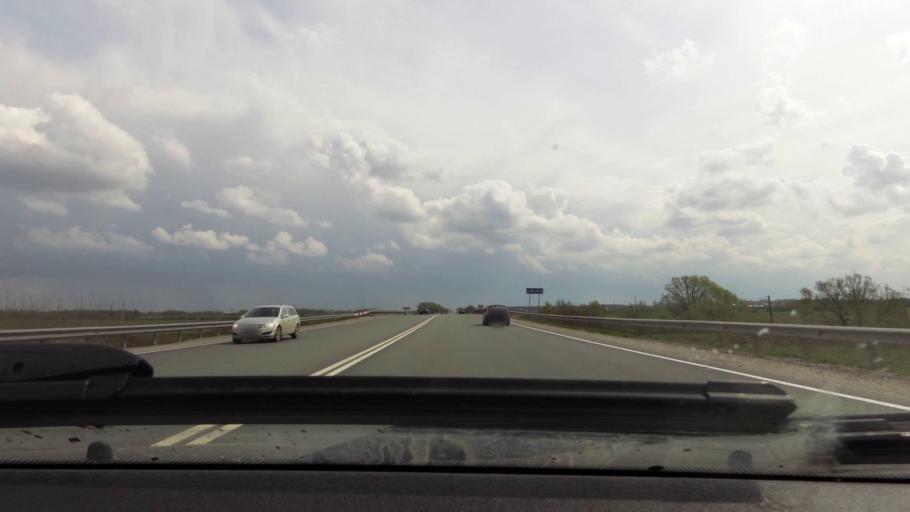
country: RU
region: Rjazan
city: Bagramovo
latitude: 54.7443
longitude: 39.4372
